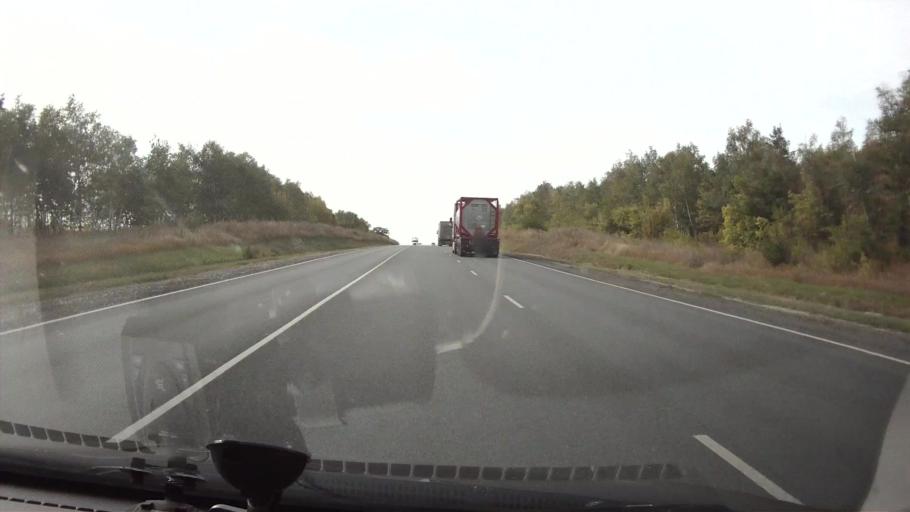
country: RU
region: Saratov
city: Tersa
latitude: 52.1021
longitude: 47.5080
